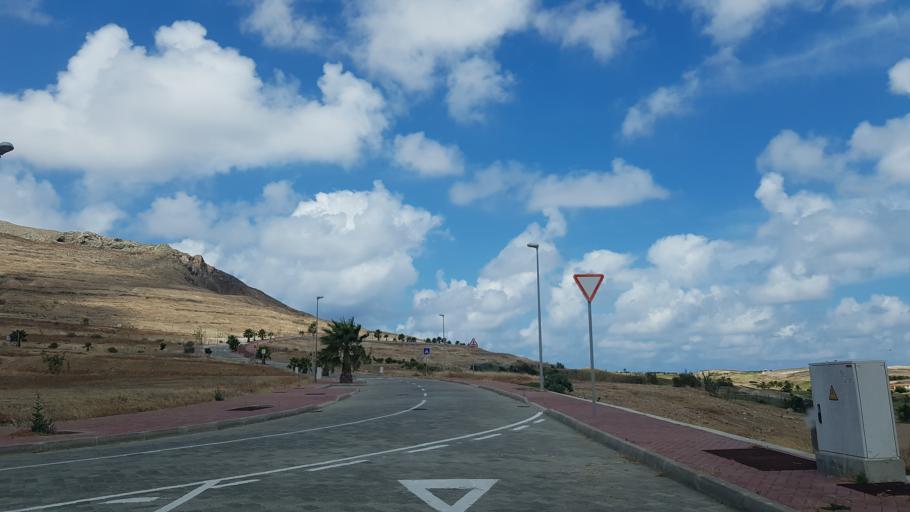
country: PT
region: Madeira
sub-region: Porto Santo
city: Vila de Porto Santo
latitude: 33.0500
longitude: -16.3630
